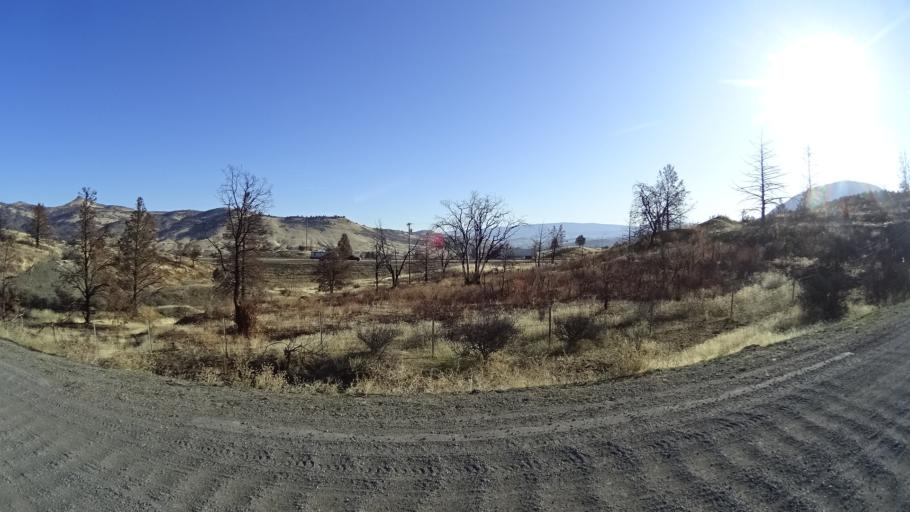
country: US
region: California
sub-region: Siskiyou County
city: Montague
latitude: 41.8977
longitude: -122.5669
